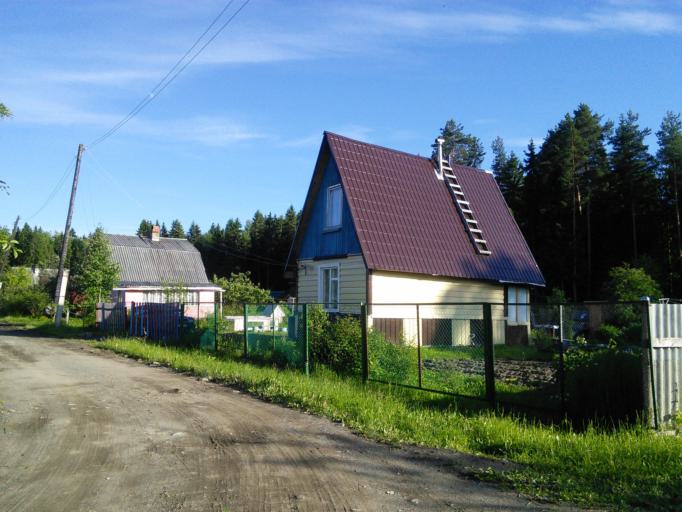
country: RU
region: Republic of Karelia
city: Shuya
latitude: 61.8498
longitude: 34.1404
